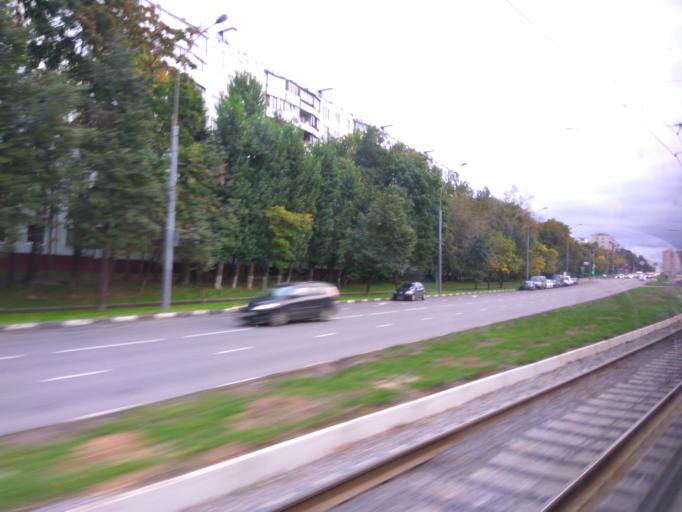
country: RU
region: Moscow
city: Nagornyy
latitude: 55.6267
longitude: 37.5973
